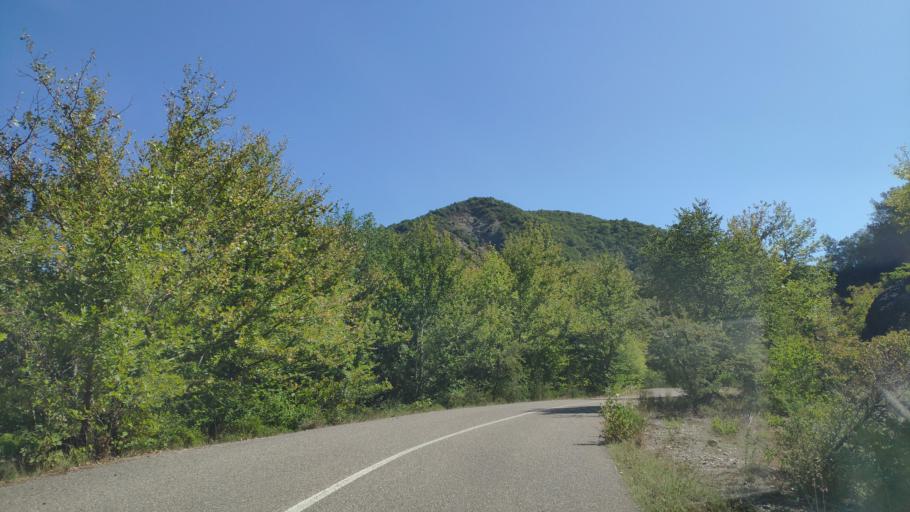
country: GR
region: Central Greece
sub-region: Nomos Evrytanias
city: Kerasochori
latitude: 39.0002
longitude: 21.5163
